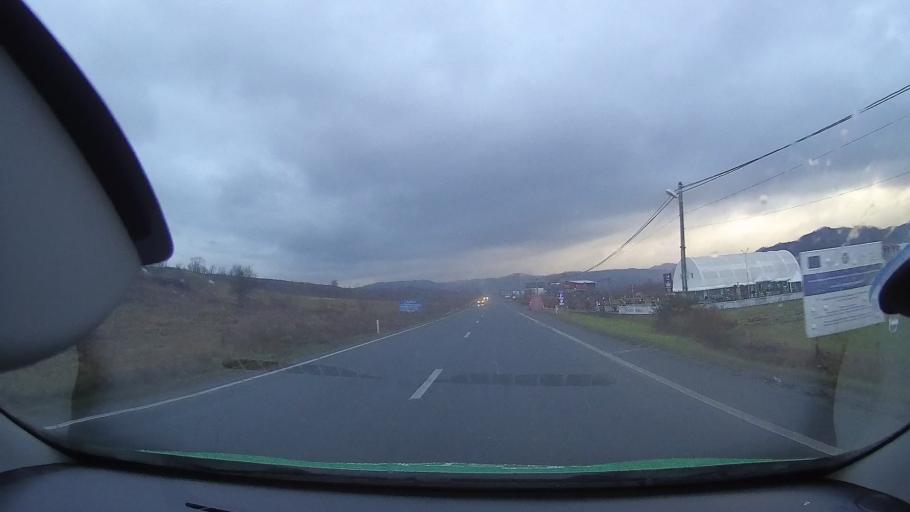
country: RO
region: Hunedoara
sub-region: Comuna Ribita
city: Ribita
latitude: 46.1562
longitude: 22.7640
